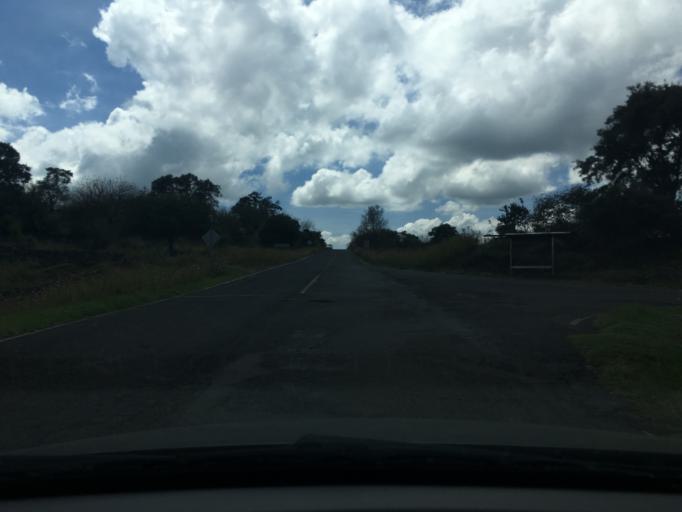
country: MX
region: Michoacan
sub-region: Morelia
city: Cuto de la Esperanza
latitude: 19.7613
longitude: -101.3716
